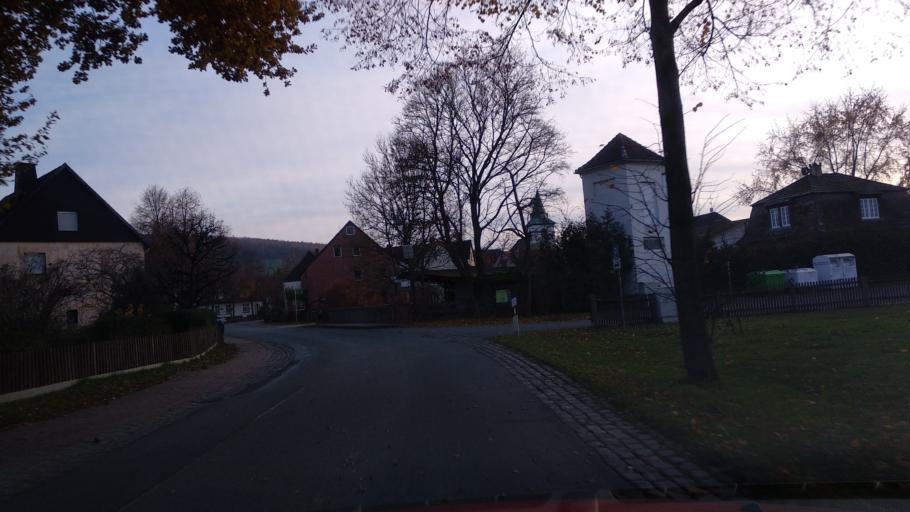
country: DE
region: Lower Saxony
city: Boffzen
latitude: 51.7144
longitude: 9.3430
